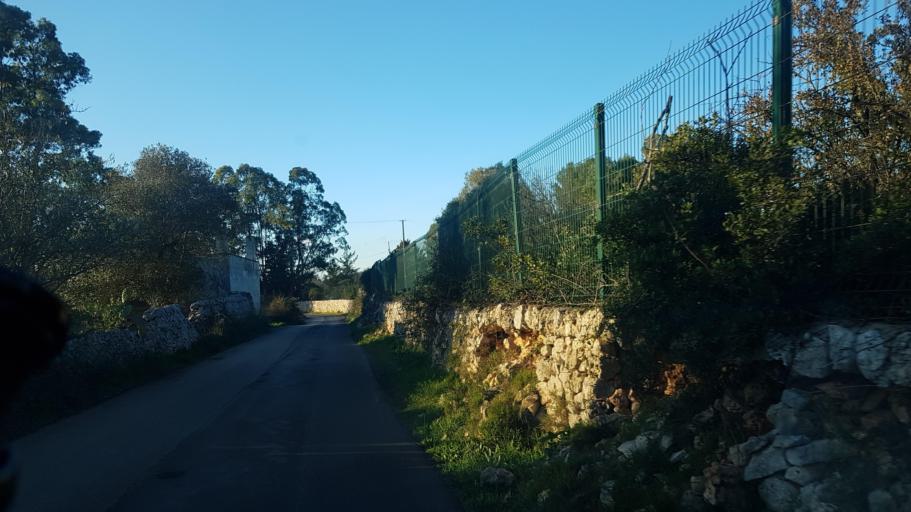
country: IT
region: Apulia
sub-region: Provincia di Brindisi
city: Ostuni
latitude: 40.7009
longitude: 17.5508
